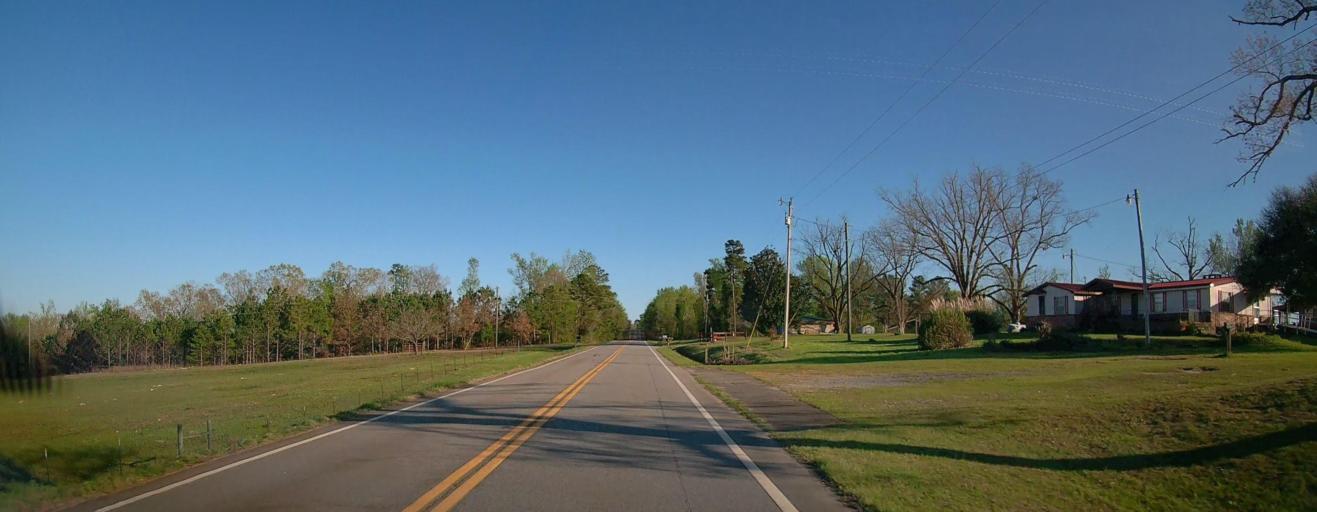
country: US
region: Georgia
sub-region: Wilkinson County
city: Irwinton
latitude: 32.9175
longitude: -83.1287
